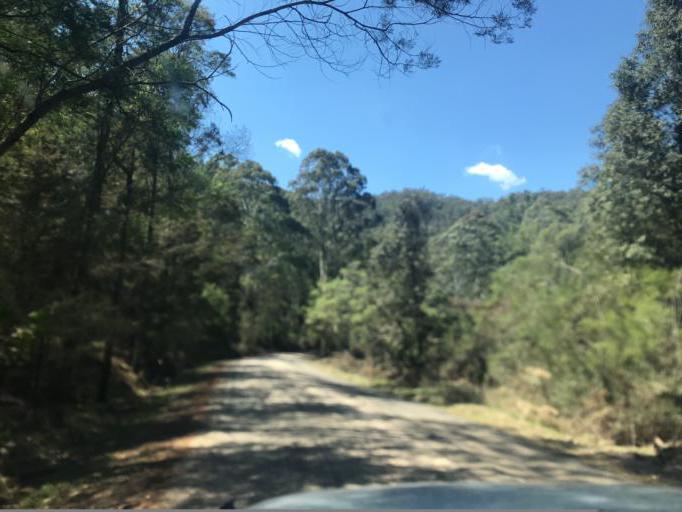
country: AU
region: New South Wales
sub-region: Wyong Shire
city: Little Jilliby
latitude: -33.1672
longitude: 151.0657
